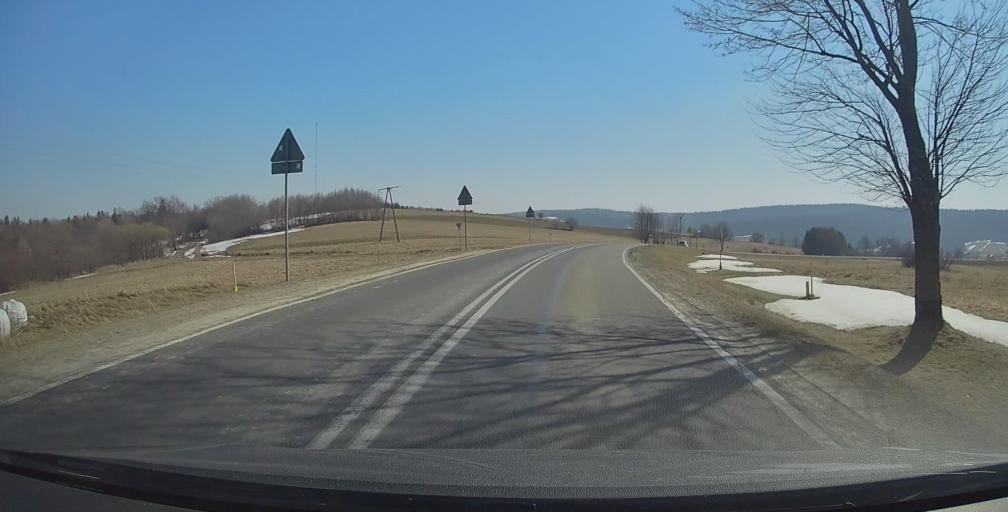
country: PL
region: Subcarpathian Voivodeship
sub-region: Powiat sanocki
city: Tyrawa Woloska
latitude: 49.6285
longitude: 22.4291
